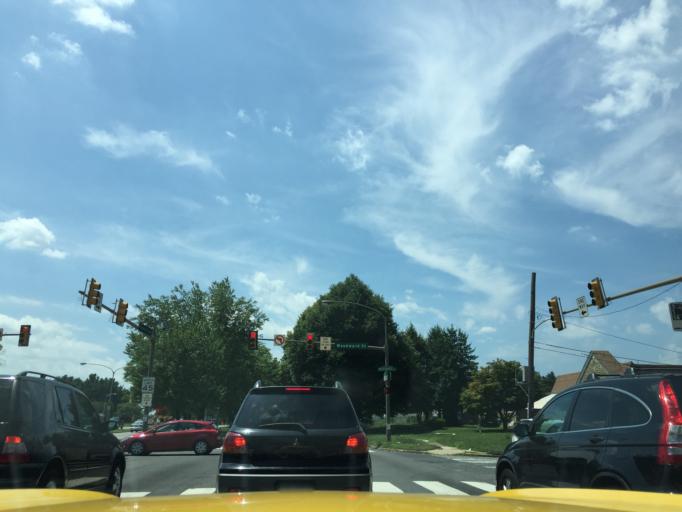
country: US
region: Pennsylvania
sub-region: Montgomery County
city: Rockledge
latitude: 40.0715
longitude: -75.0381
